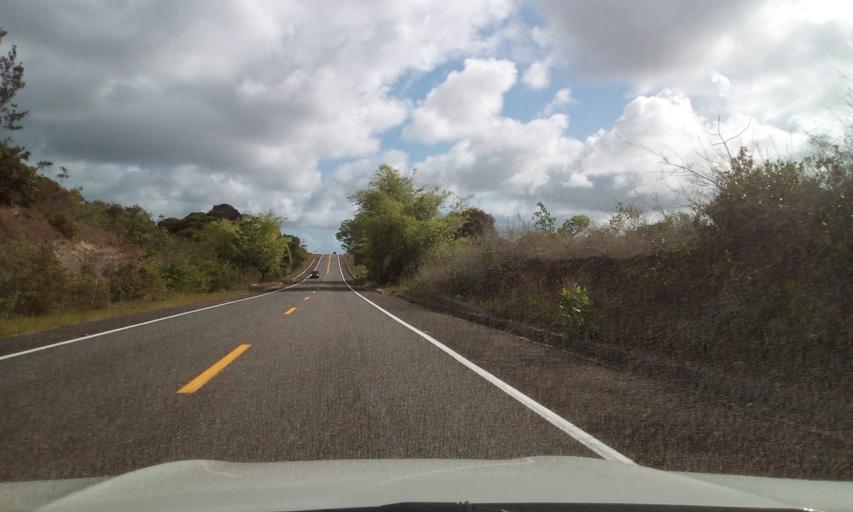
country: BR
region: Sergipe
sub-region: Indiaroba
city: Indiaroba
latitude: -11.6605
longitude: -37.5529
